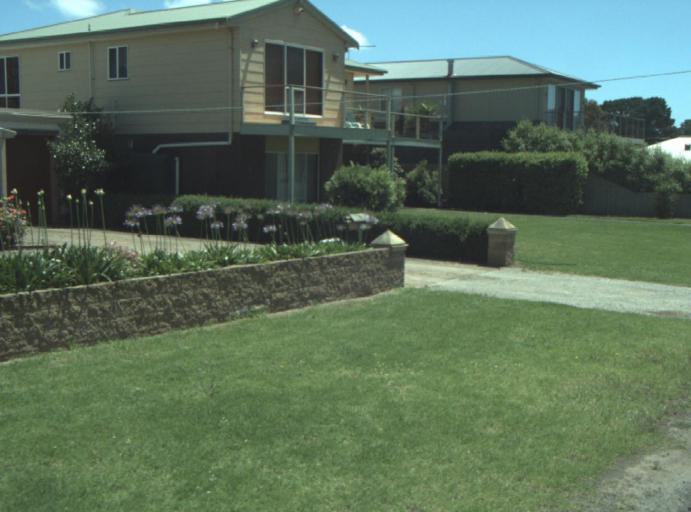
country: AU
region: Victoria
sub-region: Queenscliffe
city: Queenscliff
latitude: -38.1808
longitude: 144.7146
